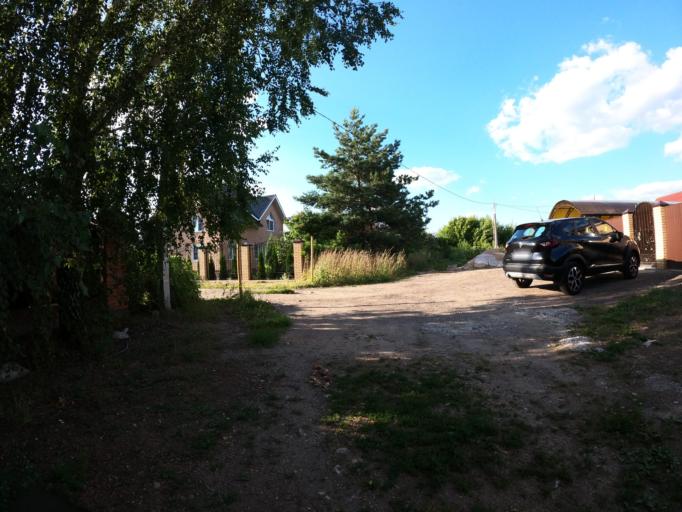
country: RU
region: Moskovskaya
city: Raduzhnyy
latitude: 55.1489
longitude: 38.7334
